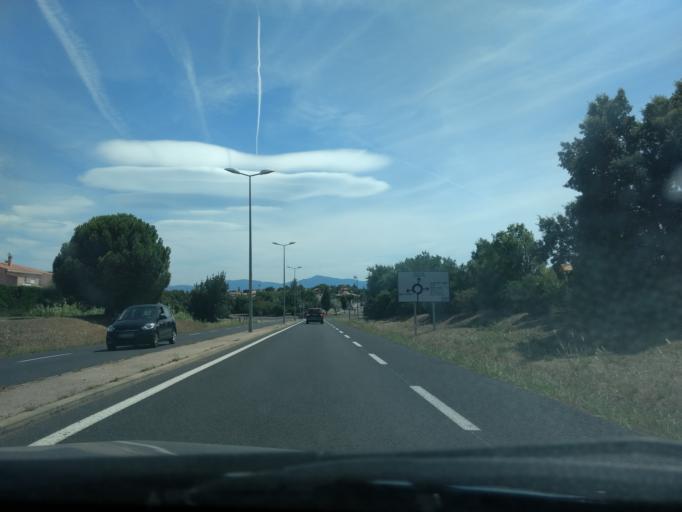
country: FR
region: Languedoc-Roussillon
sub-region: Departement des Pyrenees-Orientales
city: Cabestany
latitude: 42.6951
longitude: 2.9359
